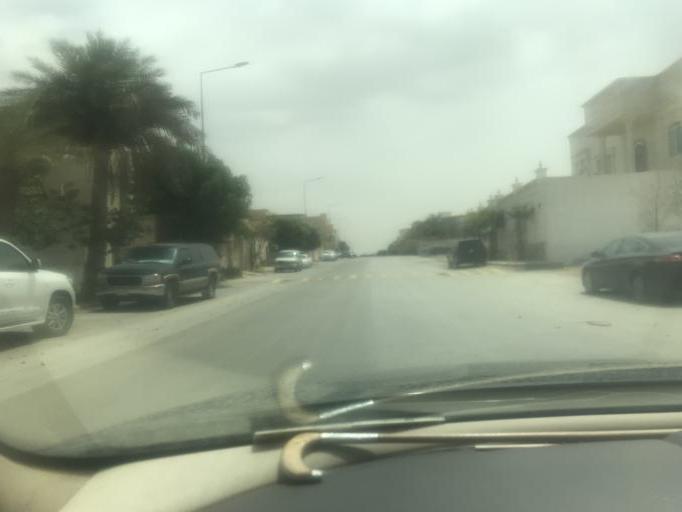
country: SA
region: Ar Riyad
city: Riyadh
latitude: 24.7898
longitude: 46.7036
